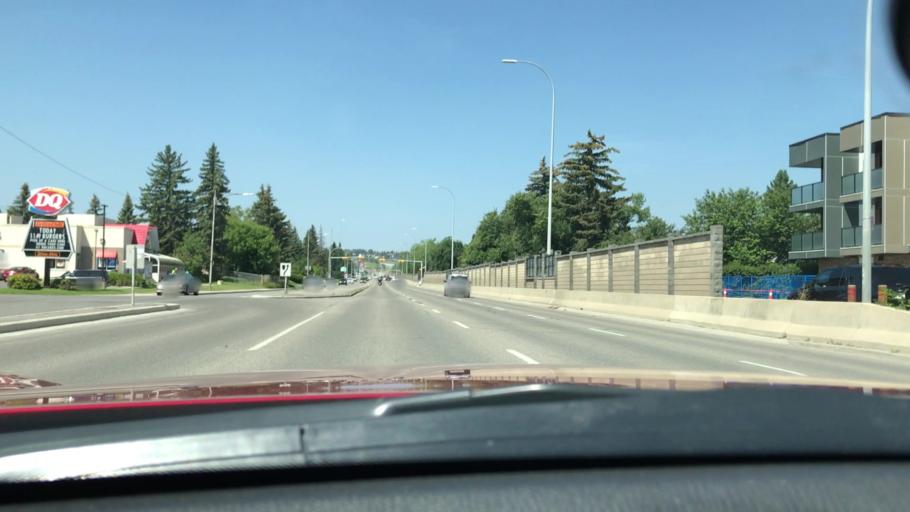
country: CA
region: Alberta
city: Calgary
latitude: 51.0461
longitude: -114.1442
